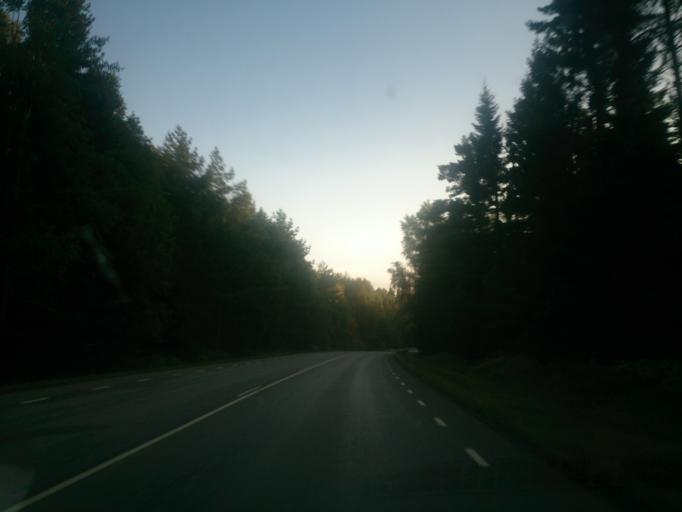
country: SE
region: Soedermanland
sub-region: Nykopings Kommun
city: Nykoping
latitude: 58.8571
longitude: 17.1338
